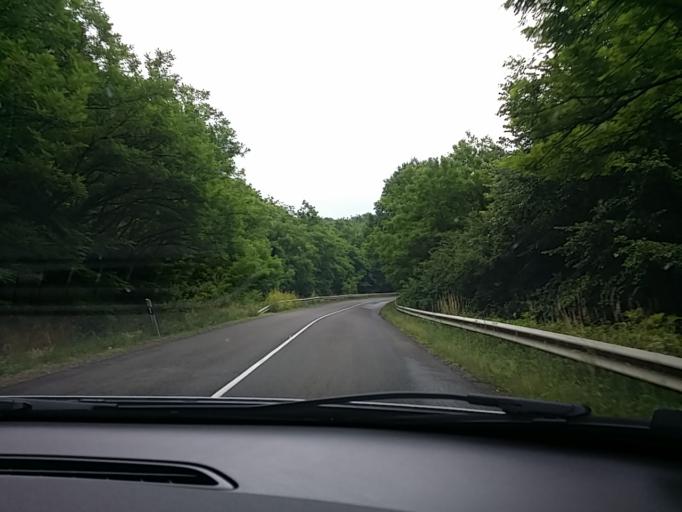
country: HU
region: Nograd
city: Matranovak
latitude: 48.0094
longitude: 19.9887
